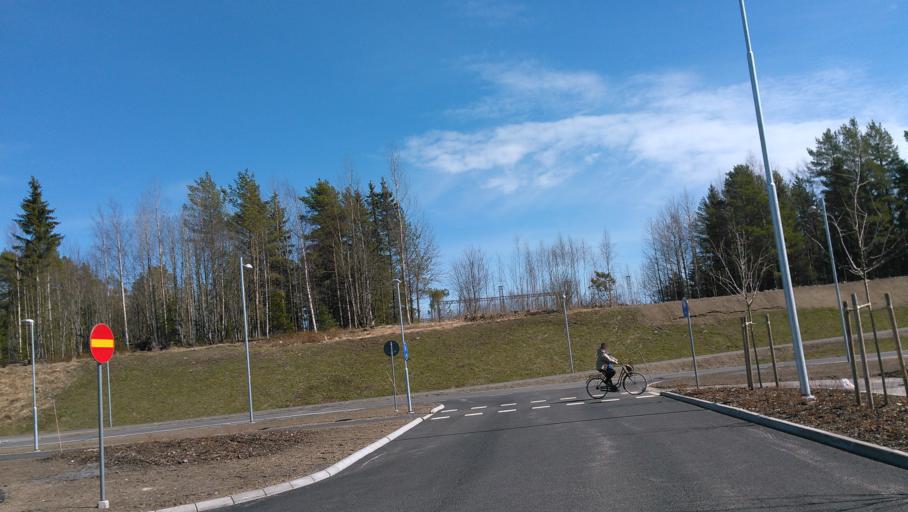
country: SE
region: Vaesterbotten
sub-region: Umea Kommun
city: Umea
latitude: 63.8075
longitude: 20.2569
